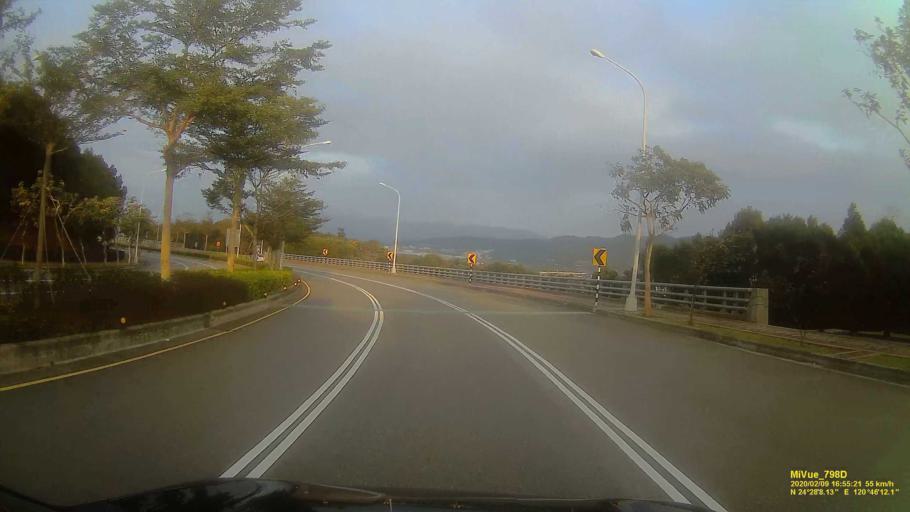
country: TW
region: Taiwan
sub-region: Miaoli
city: Miaoli
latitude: 24.4691
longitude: 120.7706
